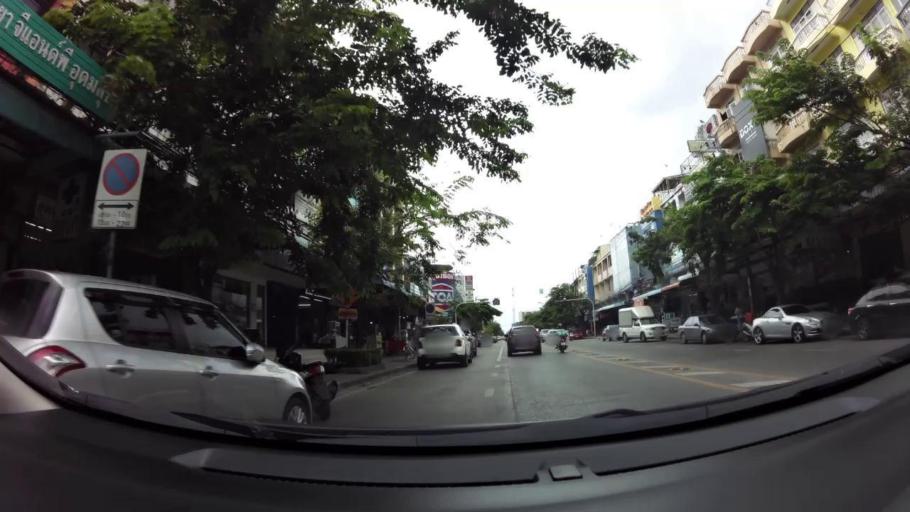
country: TH
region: Bangkok
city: Bang Na
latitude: 13.6779
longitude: 100.6338
